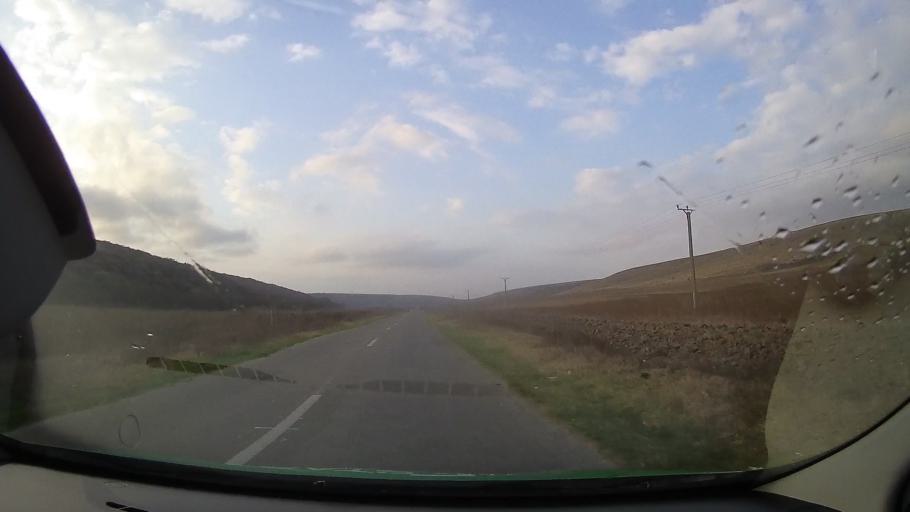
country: RO
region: Constanta
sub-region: Comuna Dobromir
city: Dobromir
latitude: 44.0271
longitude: 27.8646
